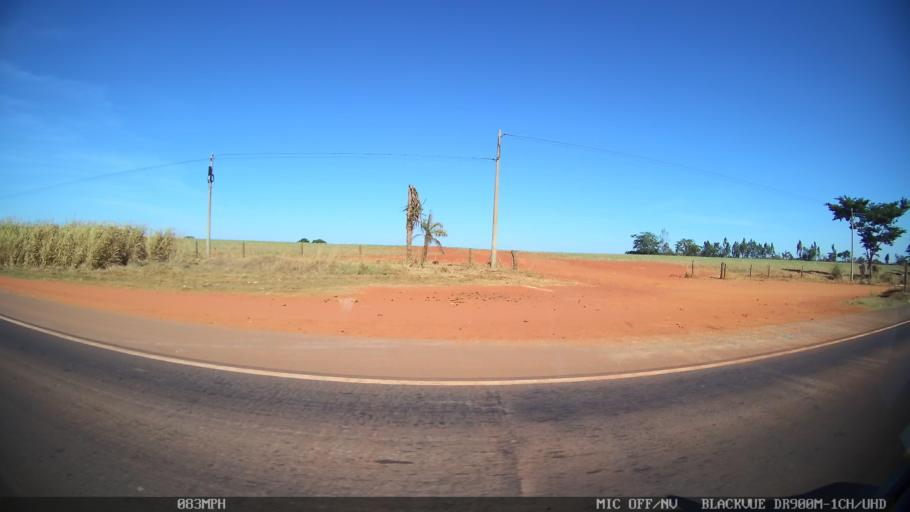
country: BR
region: Sao Paulo
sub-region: Olimpia
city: Olimpia
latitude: -20.6817
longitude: -48.8981
